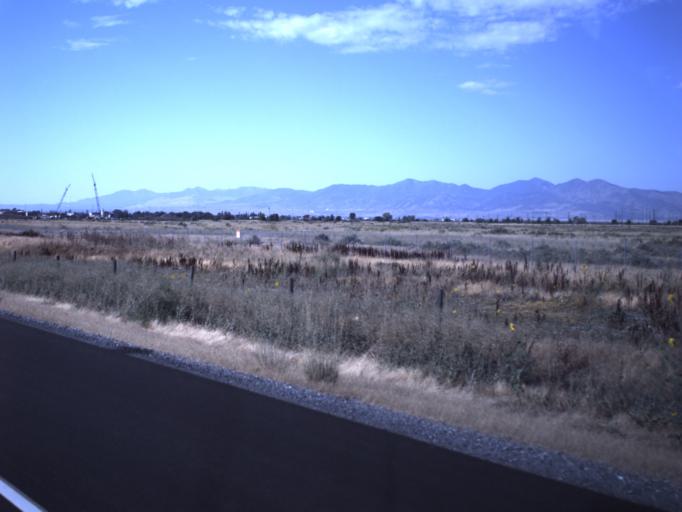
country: US
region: Utah
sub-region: Davis County
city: North Salt Lake
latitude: 40.8540
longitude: -111.9437
